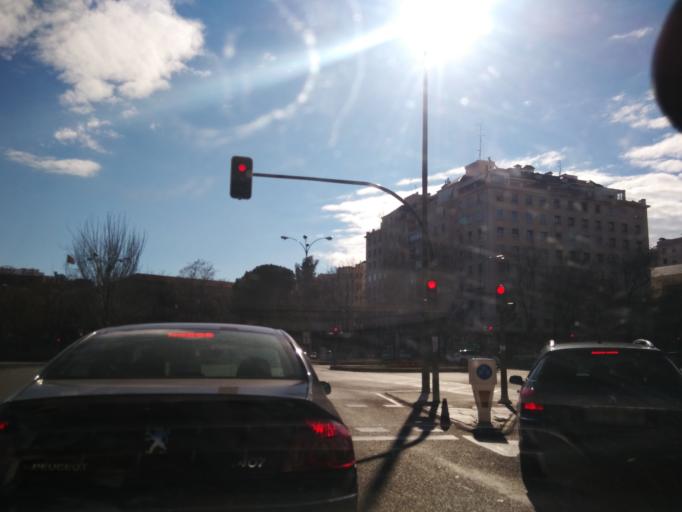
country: ES
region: Madrid
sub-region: Provincia de Madrid
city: Chamberi
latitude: 40.4417
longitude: -3.6920
